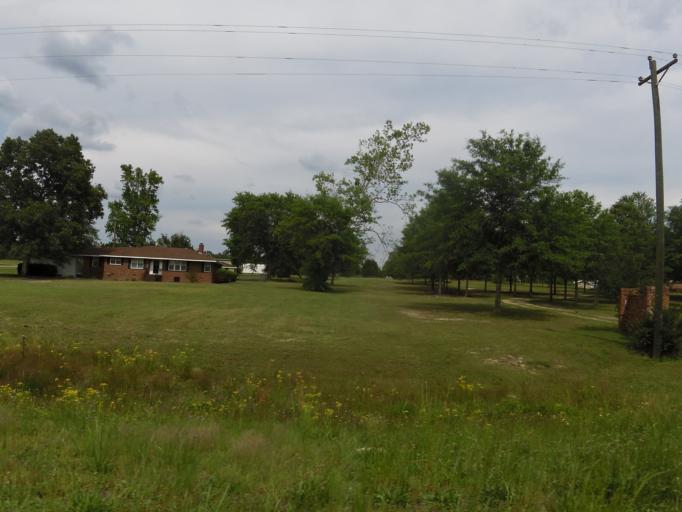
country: US
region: Georgia
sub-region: McDuffie County
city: Thomson
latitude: 33.4331
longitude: -82.4887
